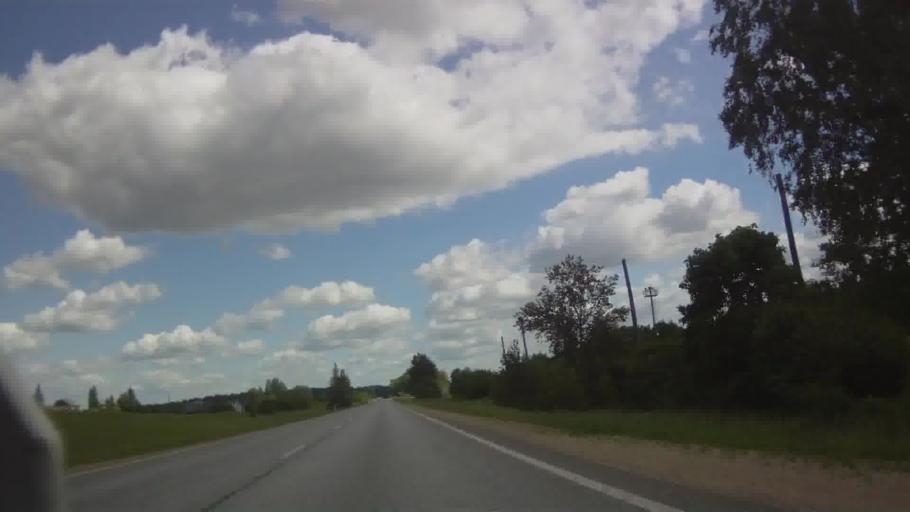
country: LV
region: Varaklani
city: Varaklani
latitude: 56.5643
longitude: 26.6275
